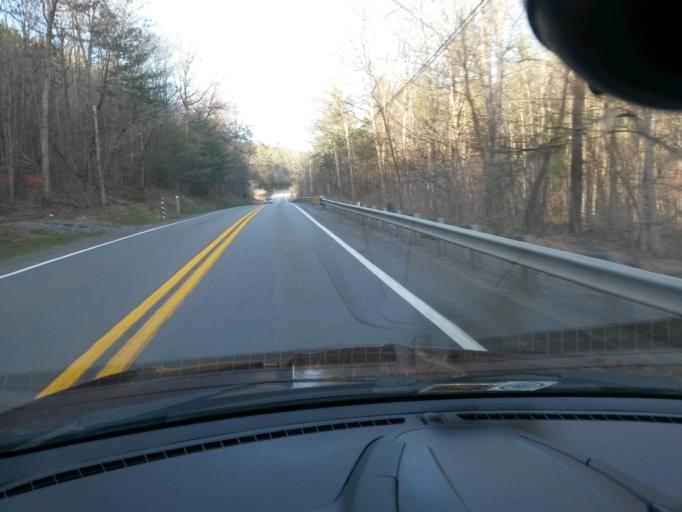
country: US
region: Virginia
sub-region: Alleghany County
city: Clifton Forge
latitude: 37.7030
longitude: -79.8156
